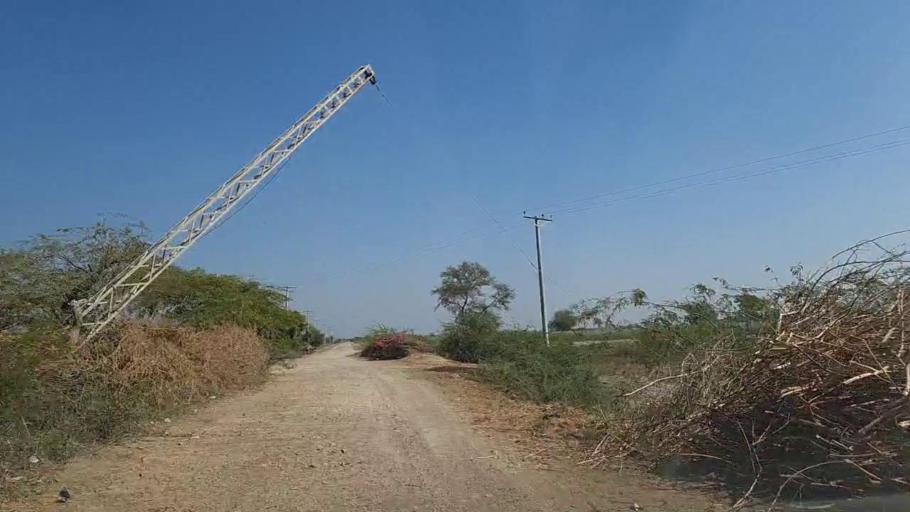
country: PK
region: Sindh
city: Pithoro
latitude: 25.4165
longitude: 69.4097
